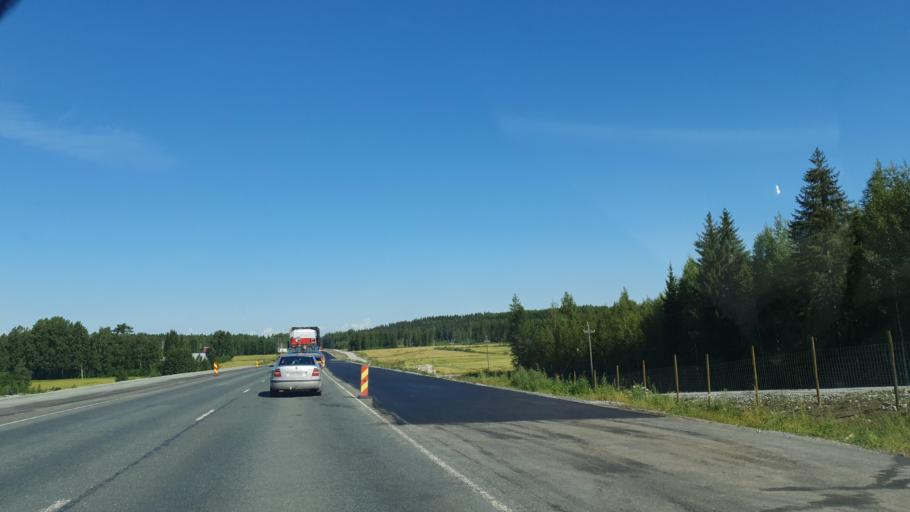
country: FI
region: Northern Savo
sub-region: Ylae-Savo
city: Lapinlahti
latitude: 63.2834
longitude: 27.4555
